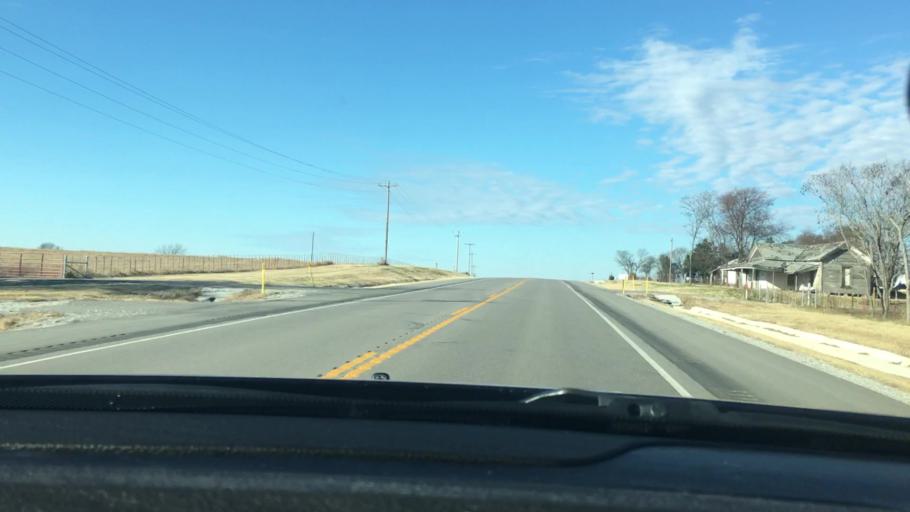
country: US
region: Oklahoma
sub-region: Love County
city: Marietta
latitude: 33.9404
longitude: -97.2021
